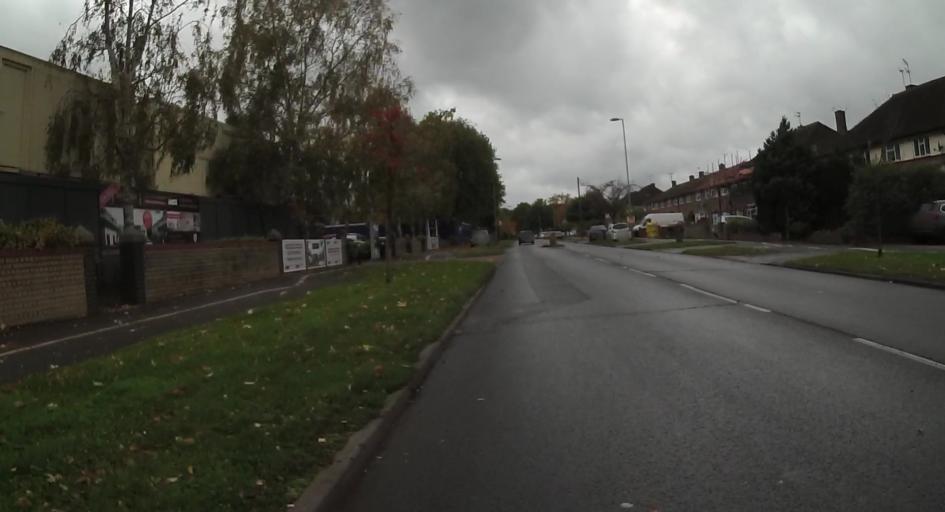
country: GB
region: England
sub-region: Surrey
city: Woking
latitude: 51.3304
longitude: -0.5346
